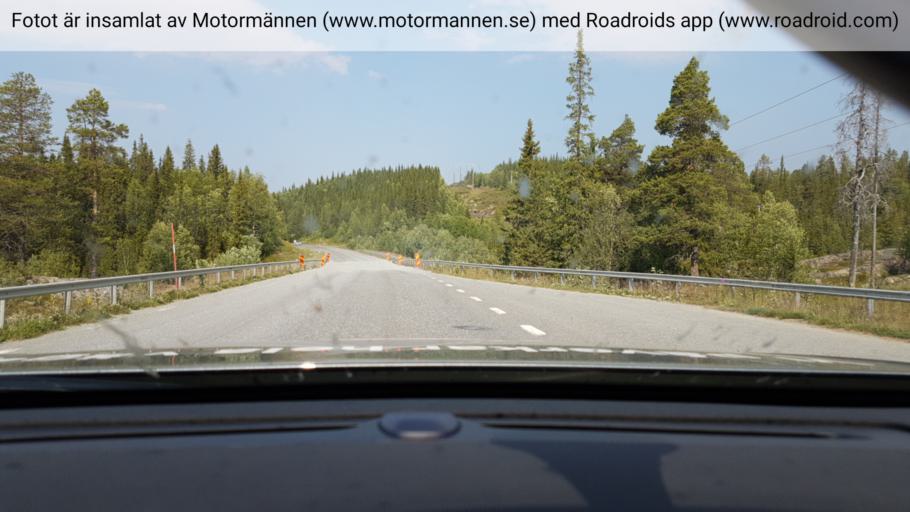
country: SE
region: Vaesterbotten
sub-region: Vilhelmina Kommun
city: Sjoberg
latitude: 65.4866
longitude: 15.8148
